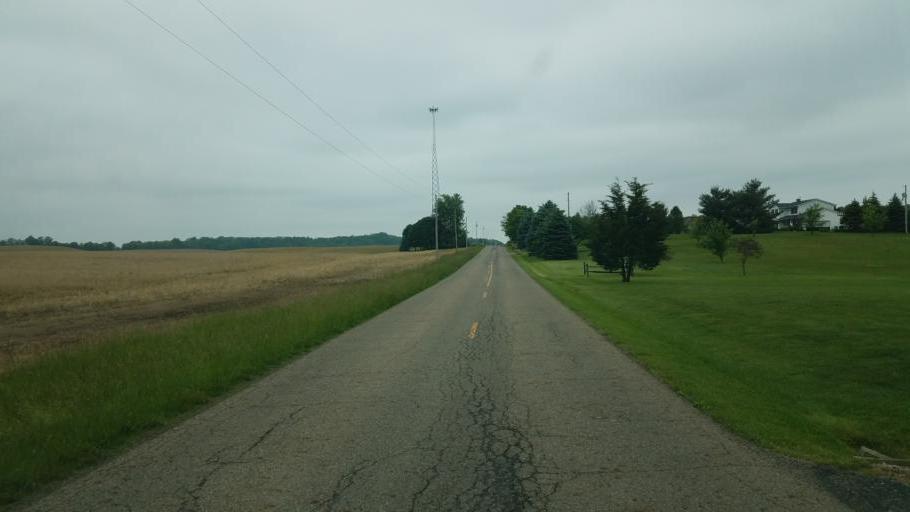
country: US
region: Ohio
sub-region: Knox County
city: Centerburg
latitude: 40.3453
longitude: -82.7258
